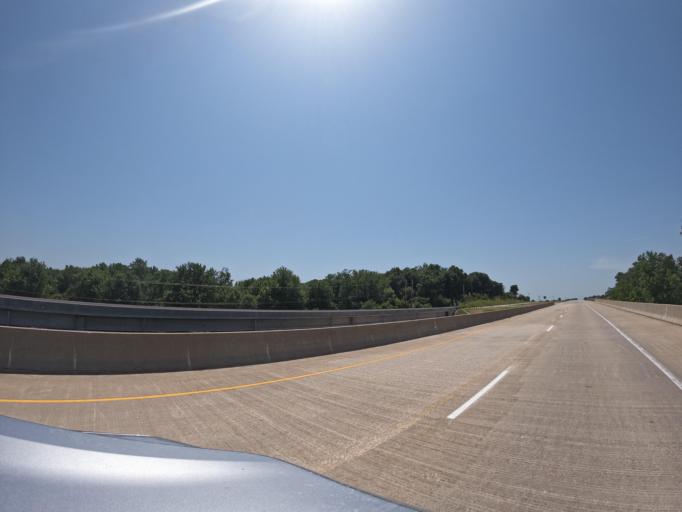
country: US
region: Iowa
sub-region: Henry County
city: Mount Pleasant
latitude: 40.9754
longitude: -91.6782
